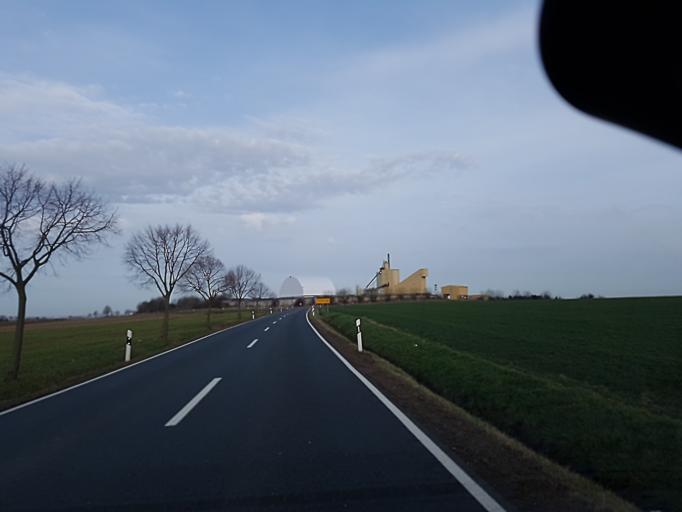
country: DE
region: Saxony
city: Bockelwitz
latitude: 51.1785
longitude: 12.9970
